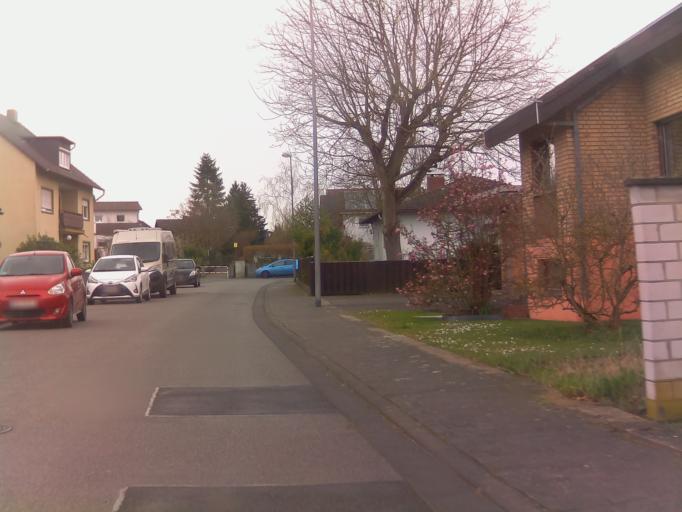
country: DE
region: Hesse
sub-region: Regierungsbezirk Darmstadt
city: Riedstadt
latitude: 49.8324
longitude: 8.4740
